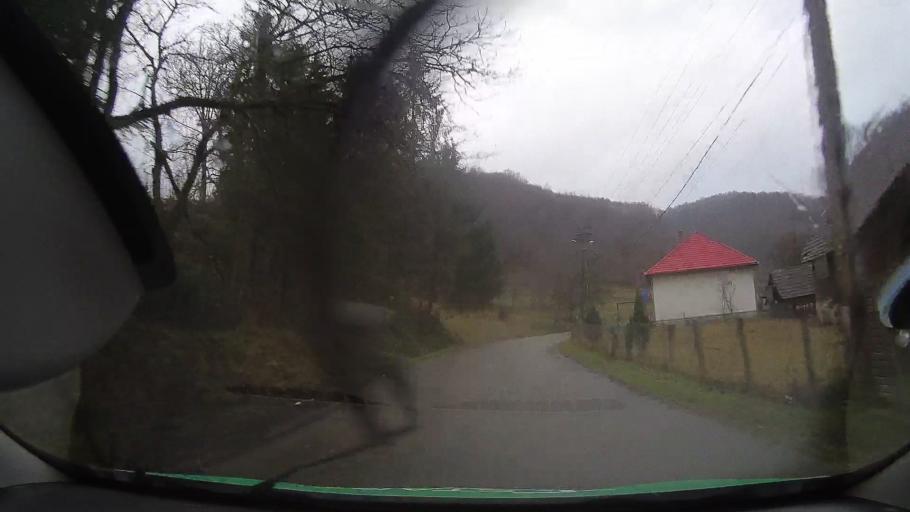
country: RO
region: Alba
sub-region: Comuna Avram Iancu
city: Avram Iancu
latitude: 46.3015
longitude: 22.7610
